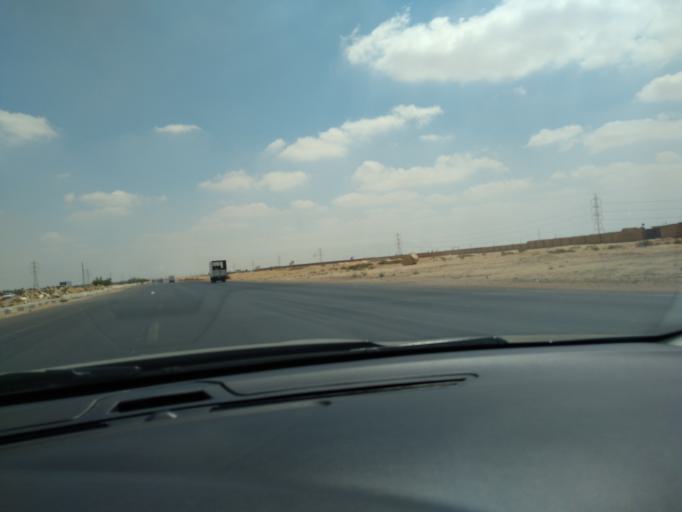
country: EG
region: Al Isma'iliyah
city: At Tall al Kabir
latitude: 30.3471
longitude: 31.8780
